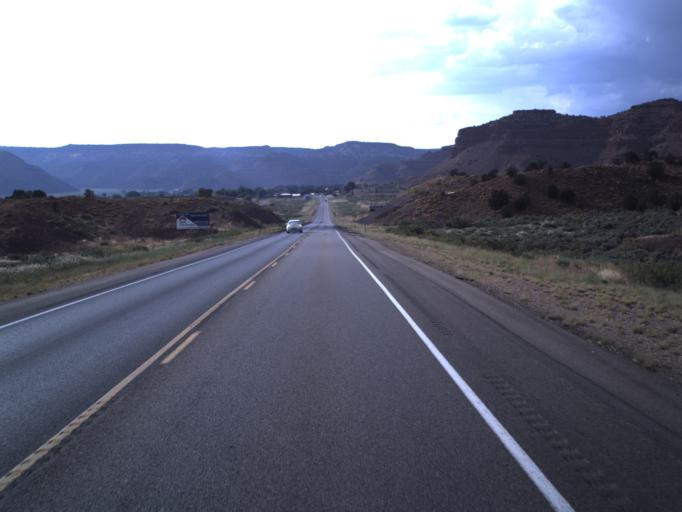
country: US
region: Utah
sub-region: Kane County
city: Kanab
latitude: 37.0342
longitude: -112.4979
